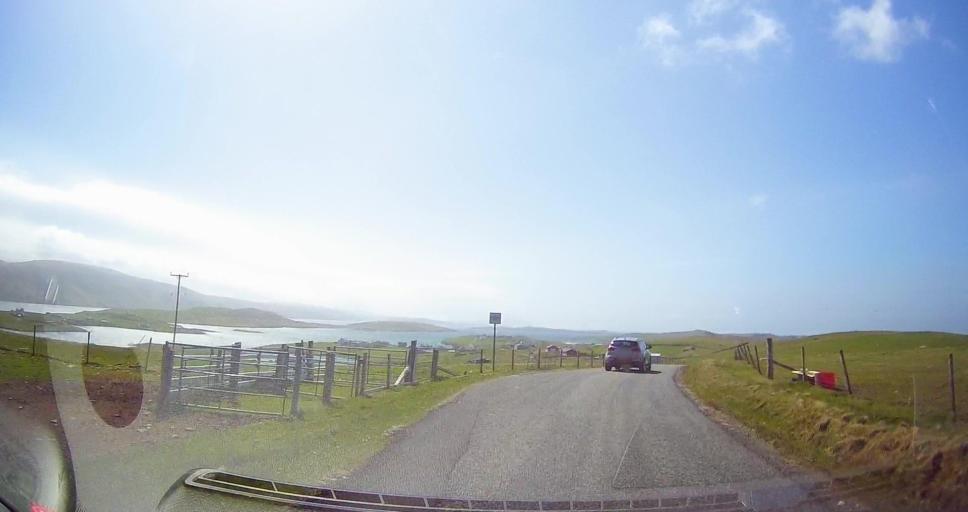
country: GB
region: Scotland
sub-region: Shetland Islands
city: Sandwick
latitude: 60.0746
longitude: -1.3381
